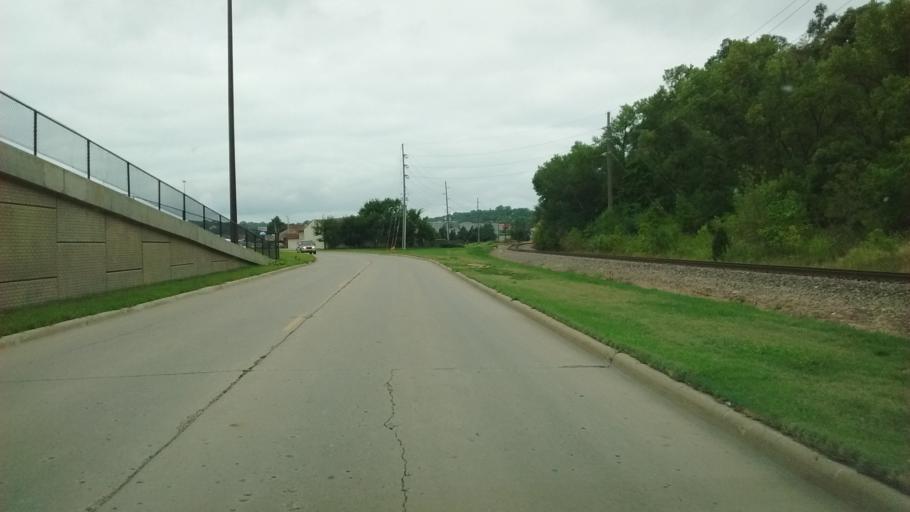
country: US
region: Iowa
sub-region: Woodbury County
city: Sioux City
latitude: 42.4923
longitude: -96.4140
